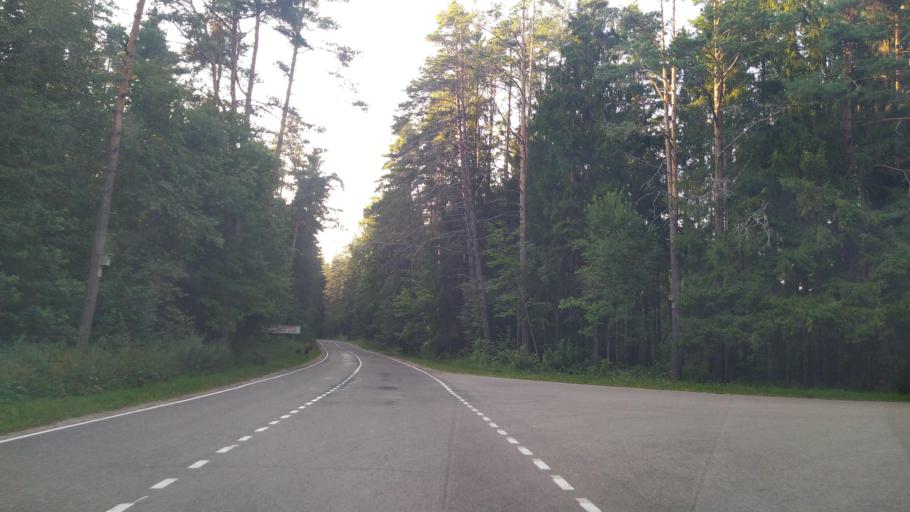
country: RU
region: Pskov
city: Pushkinskiye Gory
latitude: 57.0323
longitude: 28.9209
